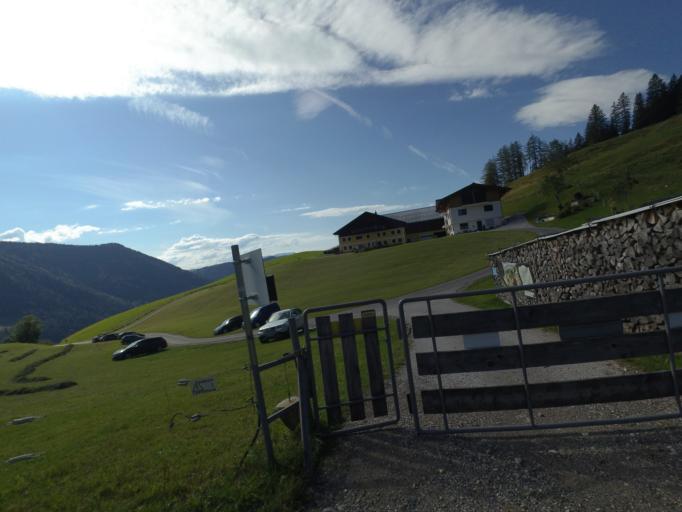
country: AT
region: Salzburg
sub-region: Politischer Bezirk Salzburg-Umgebung
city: Hintersee
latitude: 47.7026
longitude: 13.2327
